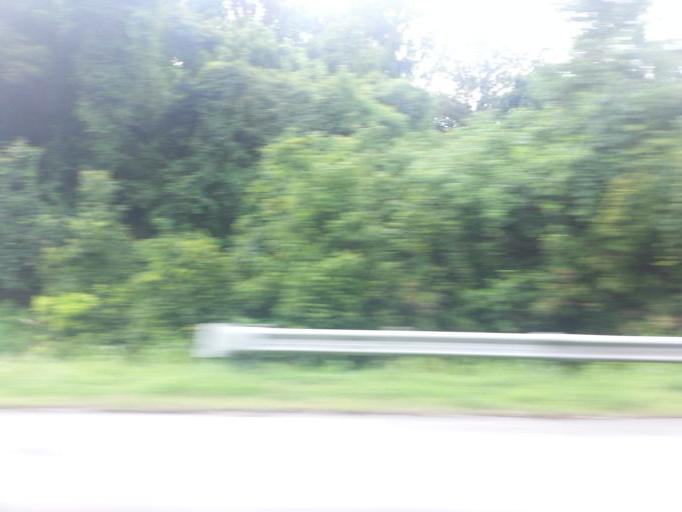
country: US
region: Tennessee
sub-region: Knox County
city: Knoxville
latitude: 36.0116
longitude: -83.8647
